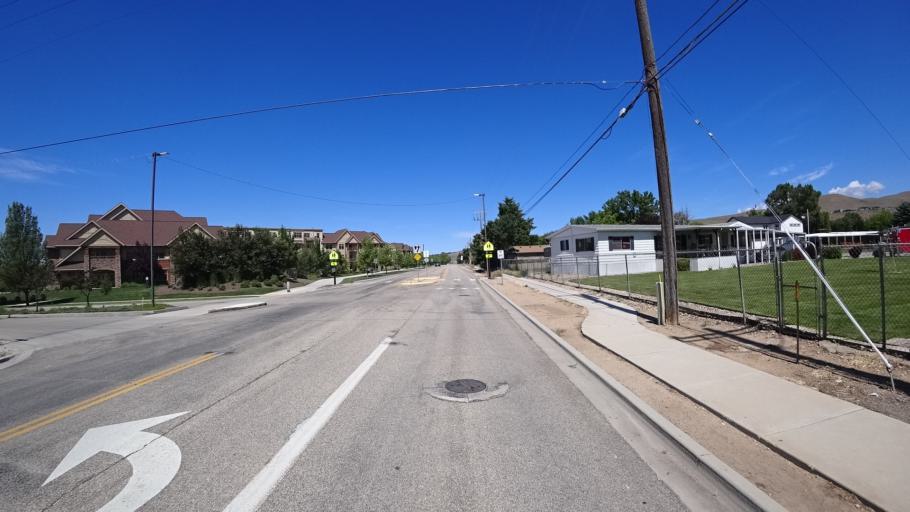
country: US
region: Idaho
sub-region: Ada County
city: Boise
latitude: 43.5662
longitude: -116.1155
